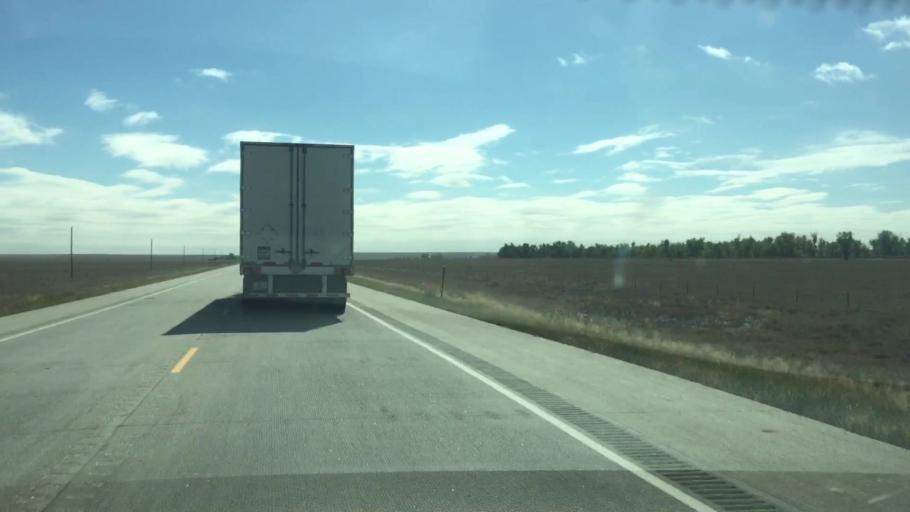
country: US
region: Colorado
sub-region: Lincoln County
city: Hugo
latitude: 39.0636
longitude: -103.3659
